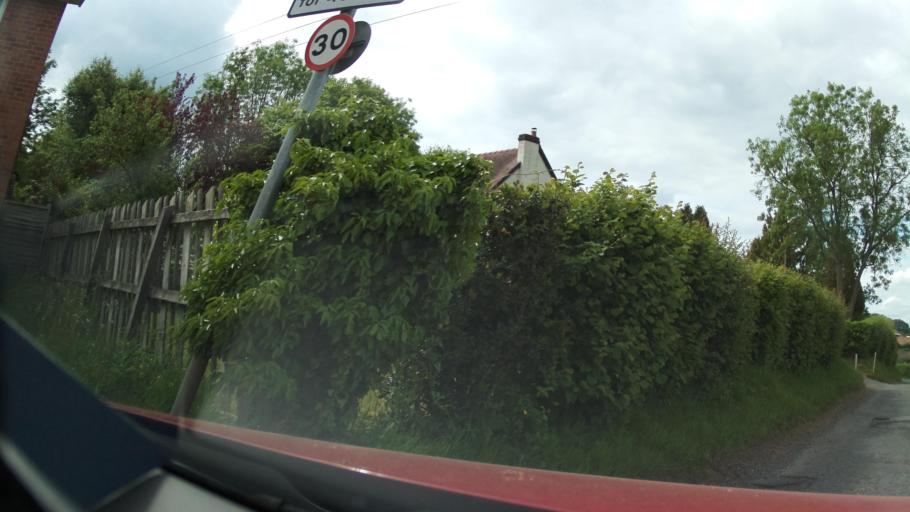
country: GB
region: England
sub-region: Herefordshire
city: Evesbatch
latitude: 52.1215
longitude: -2.4013
